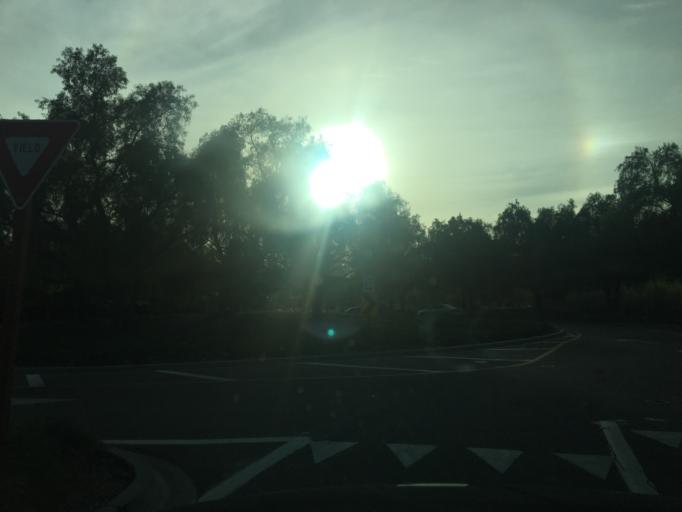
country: US
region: California
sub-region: Orange County
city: Irvine
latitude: 33.6549
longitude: -117.7808
